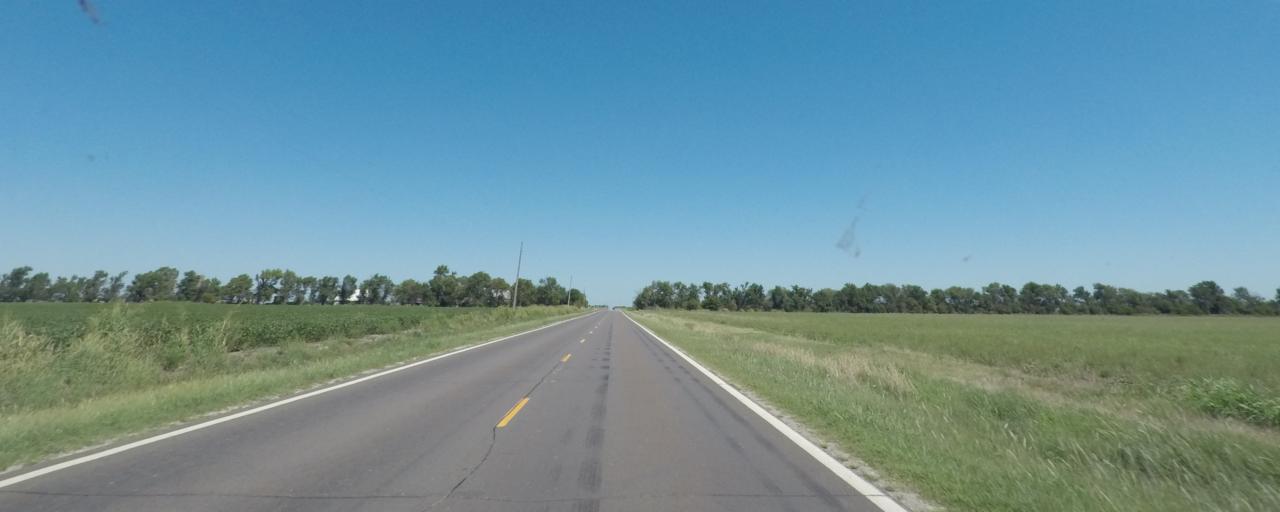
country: US
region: Kansas
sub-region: Sumner County
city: Wellington
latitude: 37.1929
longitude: -97.4022
